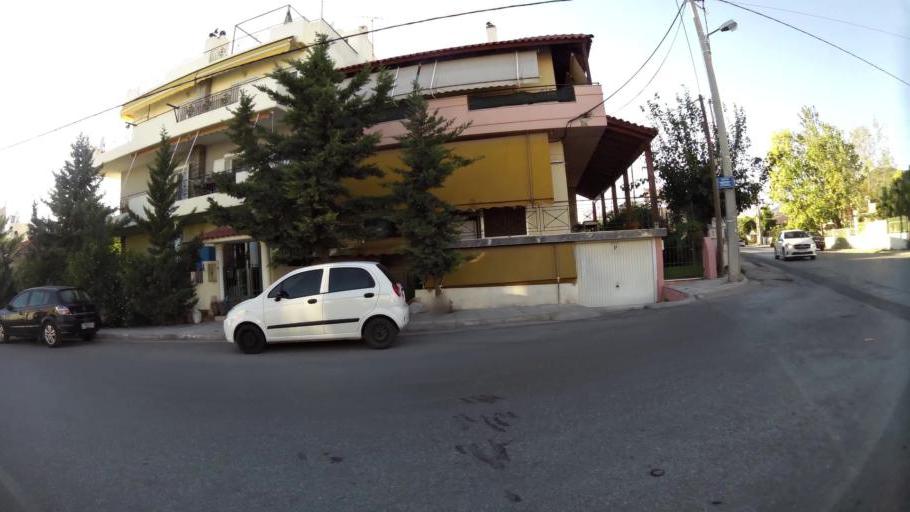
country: GR
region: Attica
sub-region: Nomarchia Anatolikis Attikis
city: Acharnes
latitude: 38.0788
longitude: 23.7247
